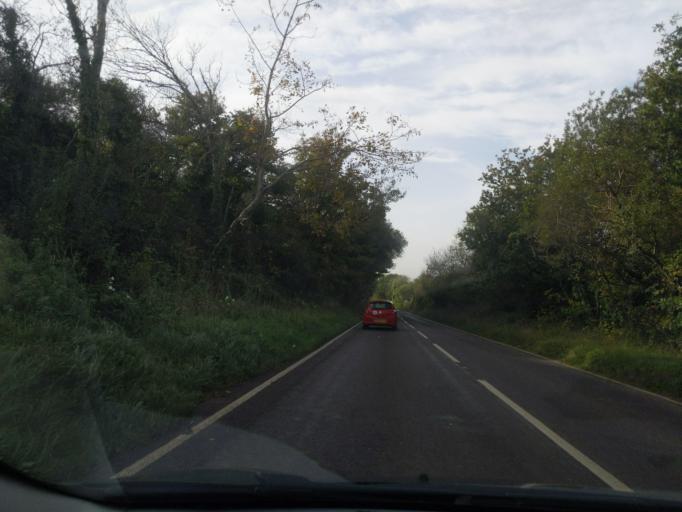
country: GB
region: England
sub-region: Cornwall
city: Saltash
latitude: 50.3742
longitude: -4.2610
